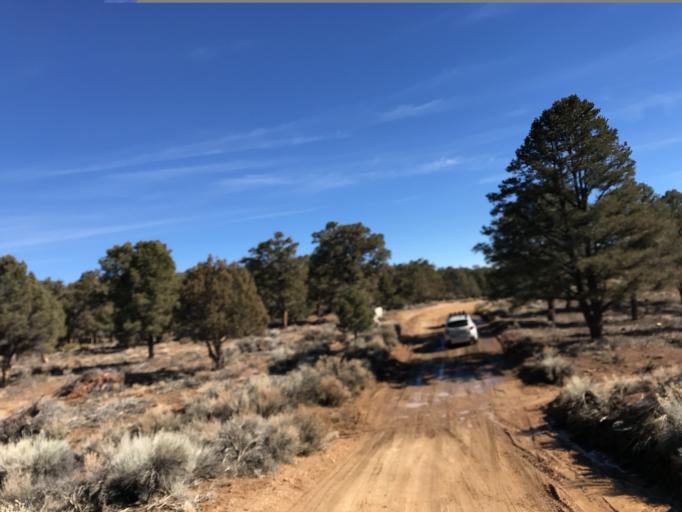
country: US
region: California
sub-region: San Bernardino County
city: Big Bear City
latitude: 34.2692
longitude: -116.7661
